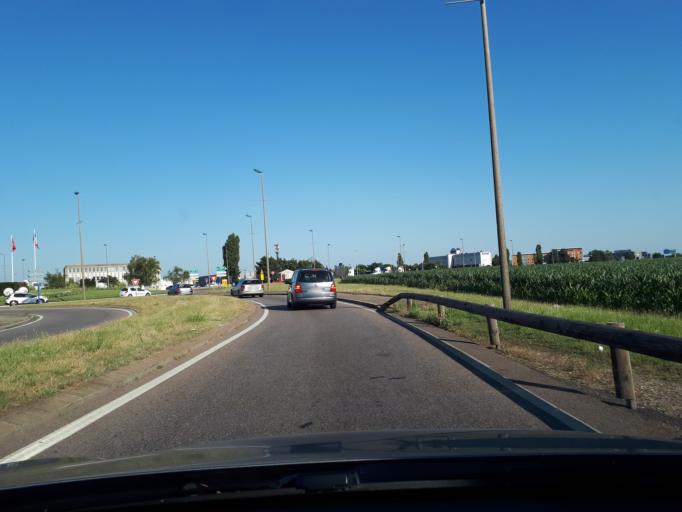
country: FR
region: Rhone-Alpes
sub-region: Departement du Rhone
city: Saint-Laurent-de-Mure
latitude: 45.7173
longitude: 5.0689
